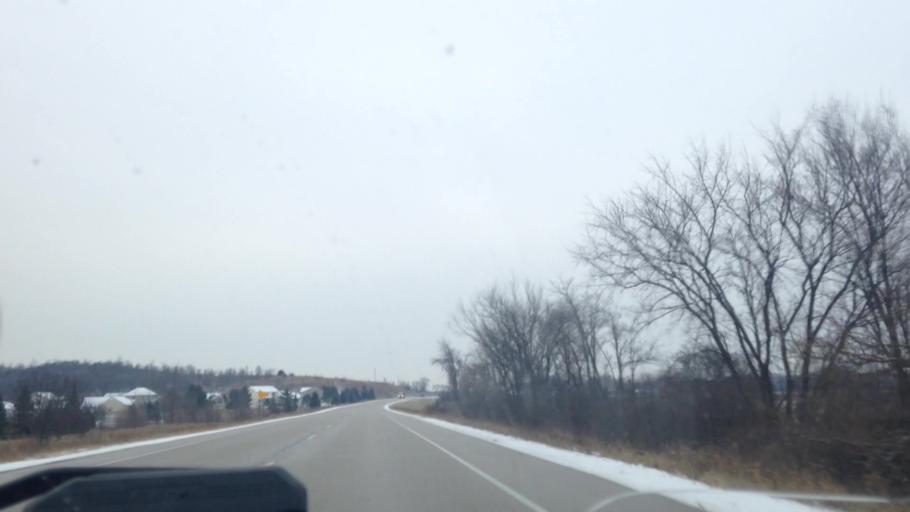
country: US
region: Wisconsin
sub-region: Waukesha County
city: Oconomowoc
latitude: 43.1721
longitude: -88.5057
